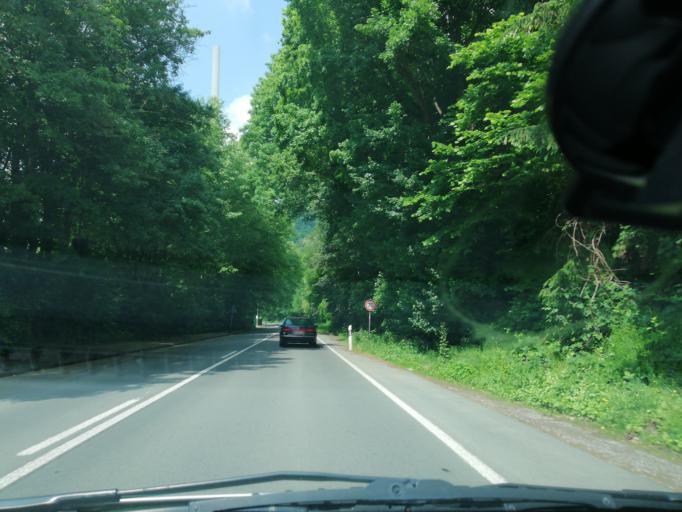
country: DE
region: North Rhine-Westphalia
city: Herdecke
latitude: 51.4027
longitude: 7.4206
